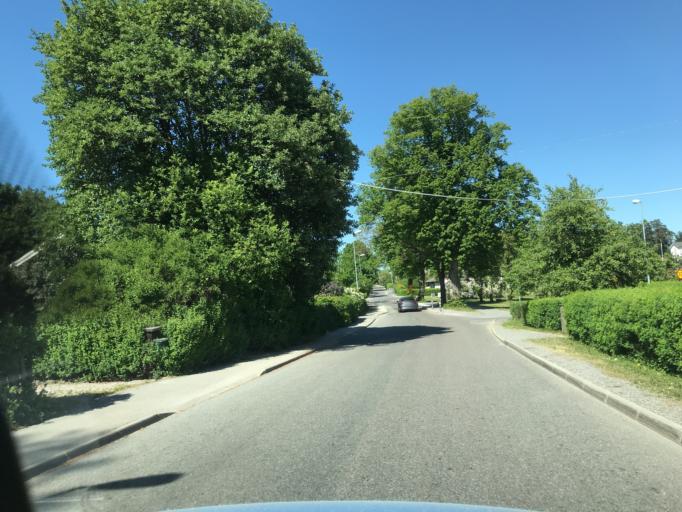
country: SE
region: Stockholm
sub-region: Sollentuna Kommun
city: Sollentuna
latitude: 59.4110
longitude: 17.9734
